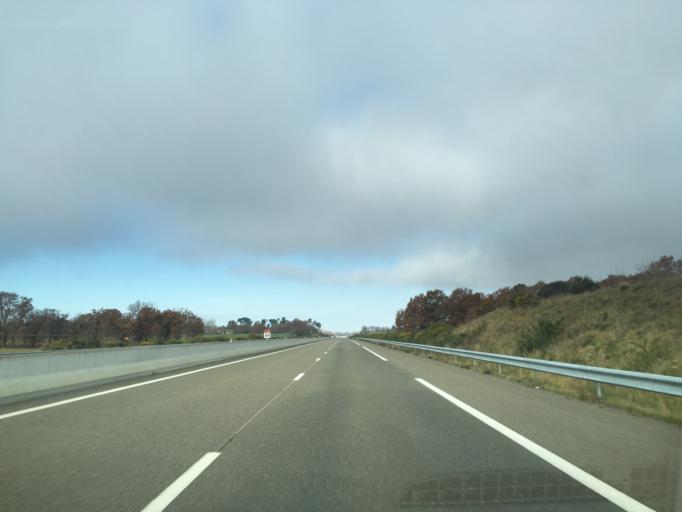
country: FR
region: Aquitaine
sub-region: Departement des Landes
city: Villeneuve-de-Marsan
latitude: 43.8363
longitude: -0.3253
